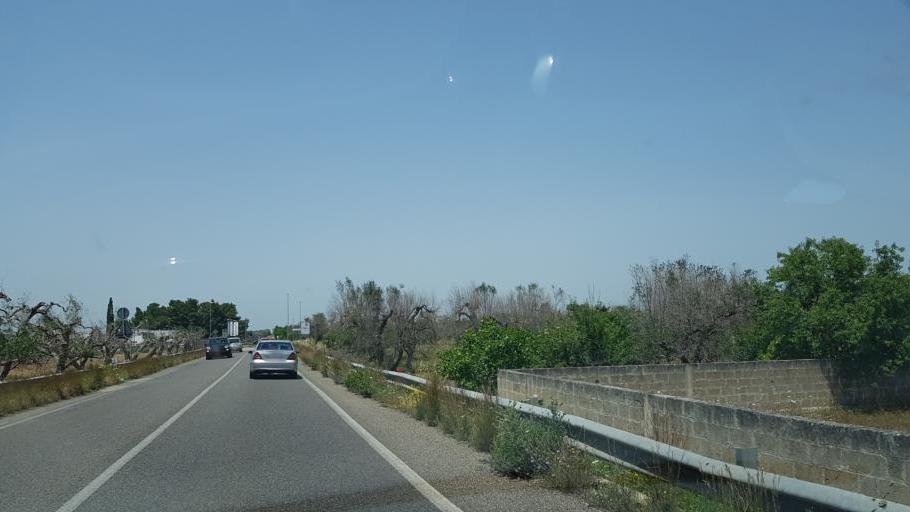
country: IT
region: Apulia
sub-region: Provincia di Lecce
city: Porto Cesareo
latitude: 40.2724
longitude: 17.9028
